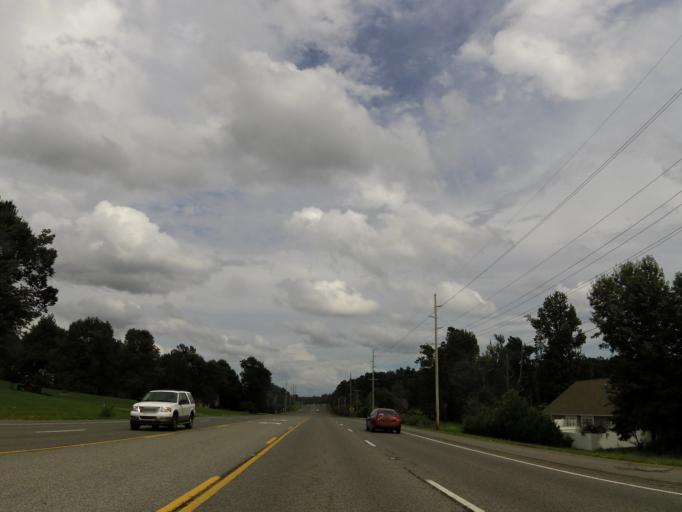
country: US
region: Kentucky
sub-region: McCracken County
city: Massac
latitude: 37.0458
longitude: -88.7011
